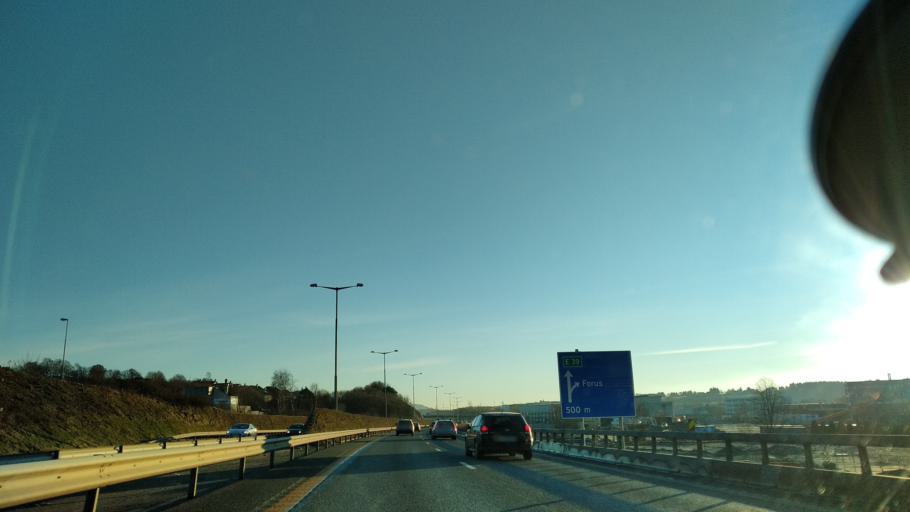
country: NO
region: Rogaland
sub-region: Sandnes
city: Sandnes
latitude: 58.8996
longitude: 5.7090
